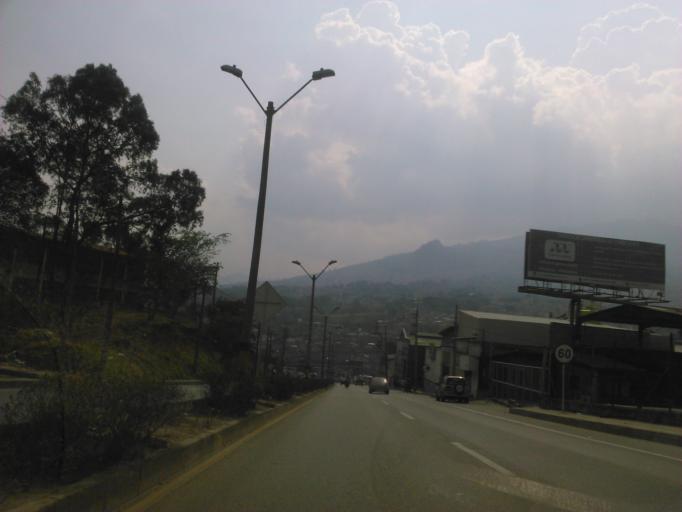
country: CO
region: Antioquia
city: Bello
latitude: 6.3106
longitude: -75.5523
